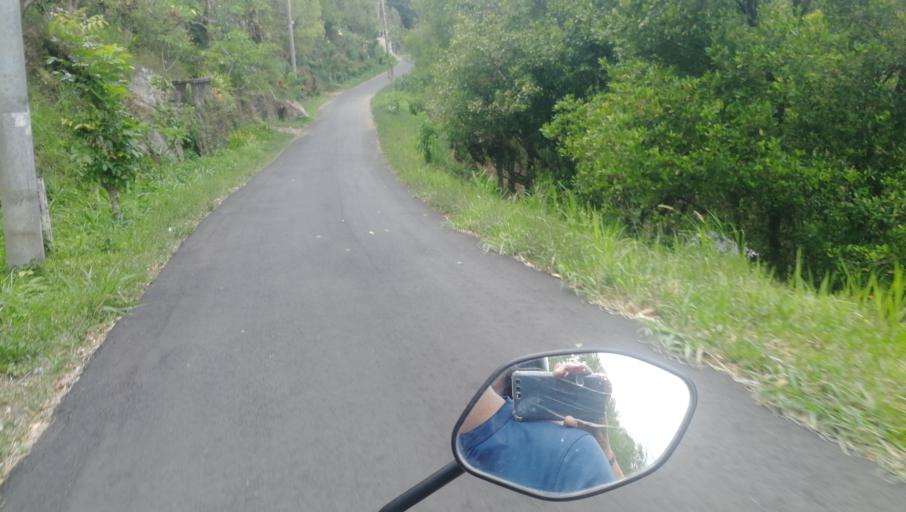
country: ID
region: Bali
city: Munduk
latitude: -8.2861
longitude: 115.0382
